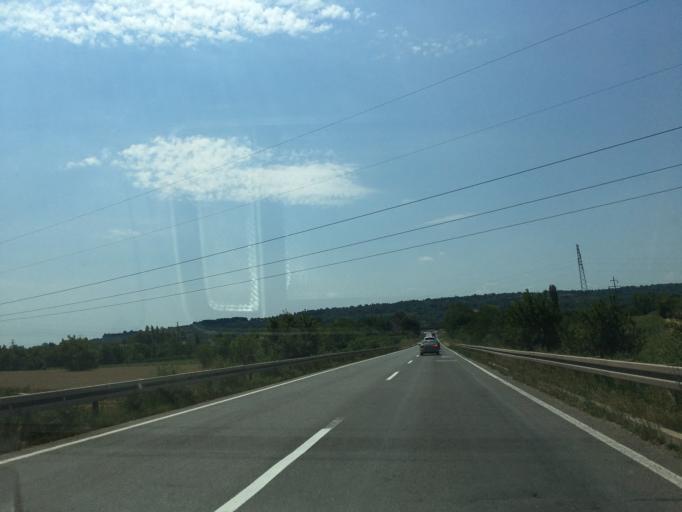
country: RS
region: Central Serbia
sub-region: Podunavski Okrug
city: Smederevo
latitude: 44.5957
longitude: 20.9563
